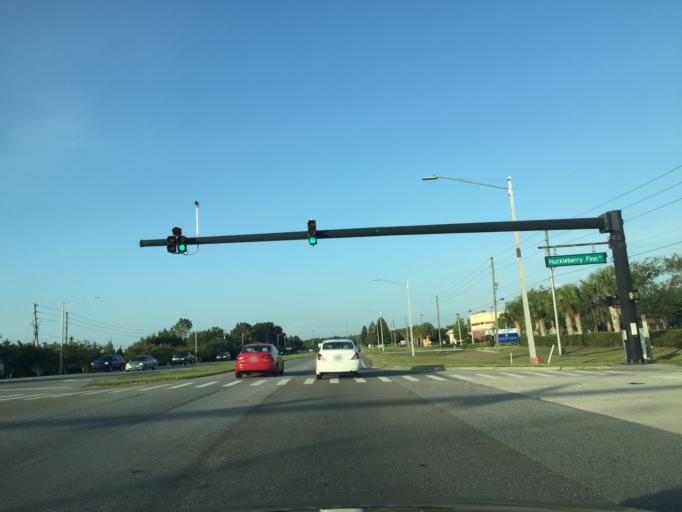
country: US
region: Florida
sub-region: Orange County
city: Alafaya
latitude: 28.5431
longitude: -81.2049
